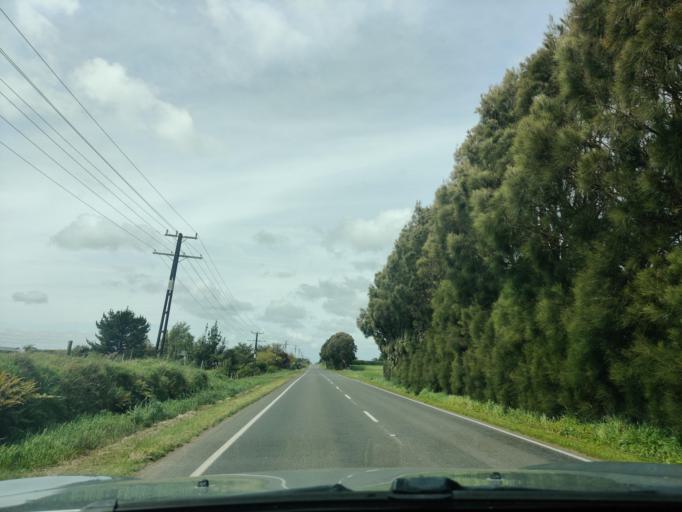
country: NZ
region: Taranaki
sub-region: South Taranaki District
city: Eltham
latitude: -39.4284
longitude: 174.1588
